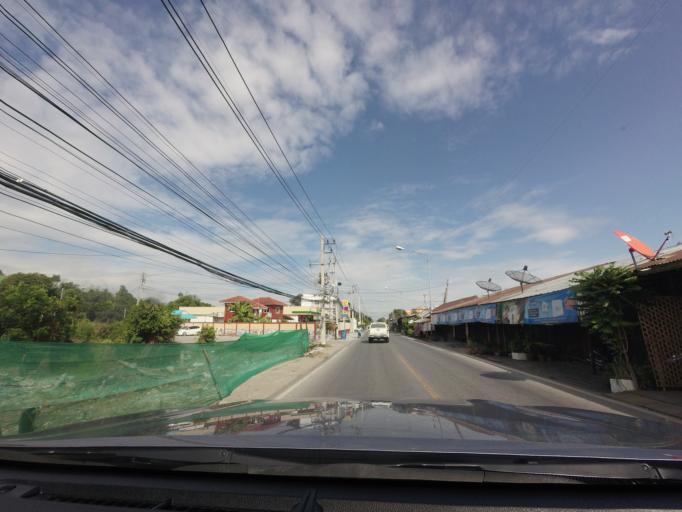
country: TH
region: Suphan Buri
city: Suphan Buri
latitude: 14.5369
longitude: 100.1247
